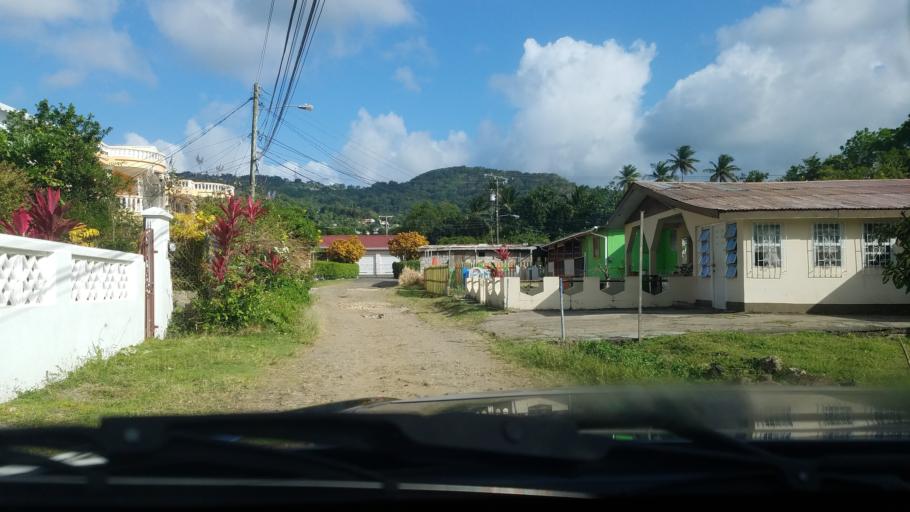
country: LC
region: Castries Quarter
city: Bisee
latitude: 14.0366
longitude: -60.9499
